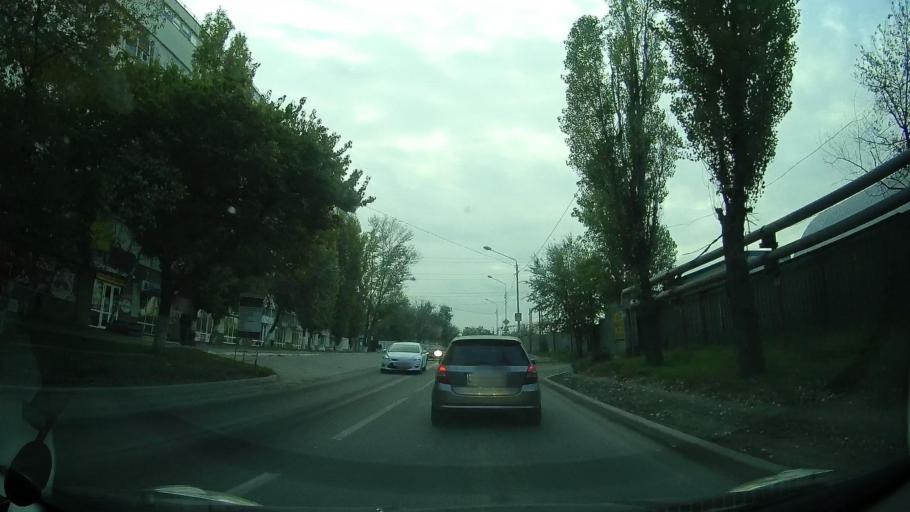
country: RU
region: Rostov
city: Rostov-na-Donu
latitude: 47.2428
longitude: 39.6698
